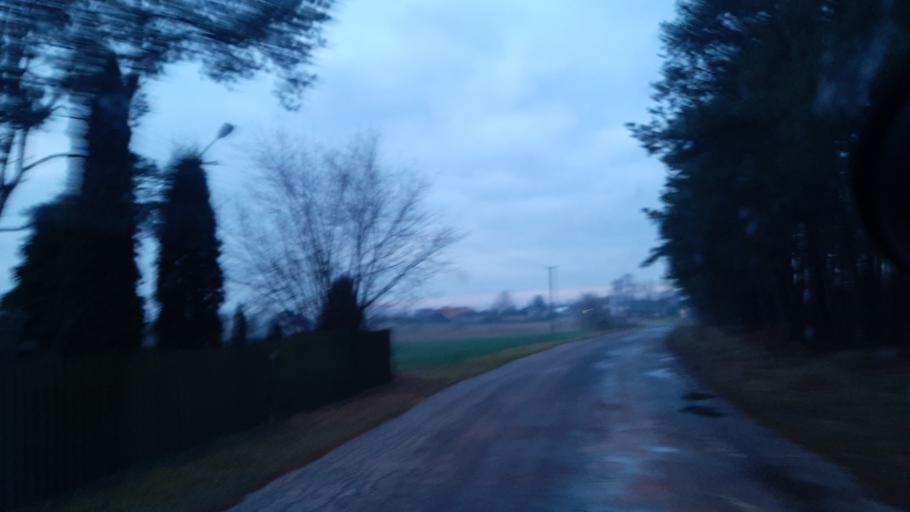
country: PL
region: Lublin Voivodeship
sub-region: Powiat lubartowski
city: Firlej
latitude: 51.5997
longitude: 22.5156
